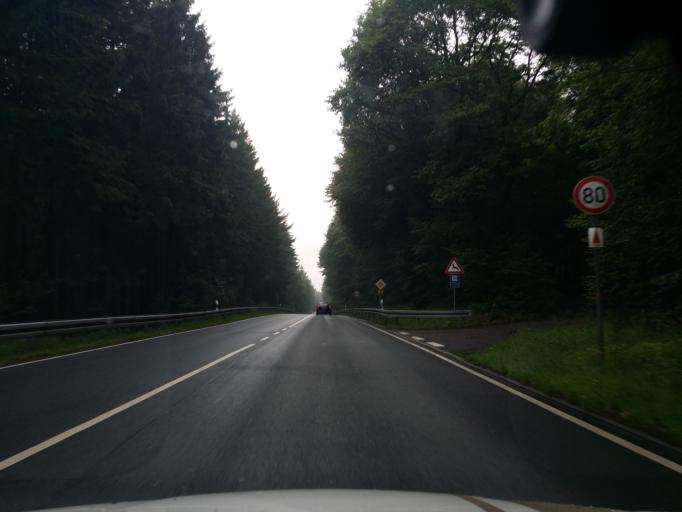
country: DE
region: Hesse
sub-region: Regierungsbezirk Darmstadt
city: Glashutten
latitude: 50.2100
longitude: 8.4134
